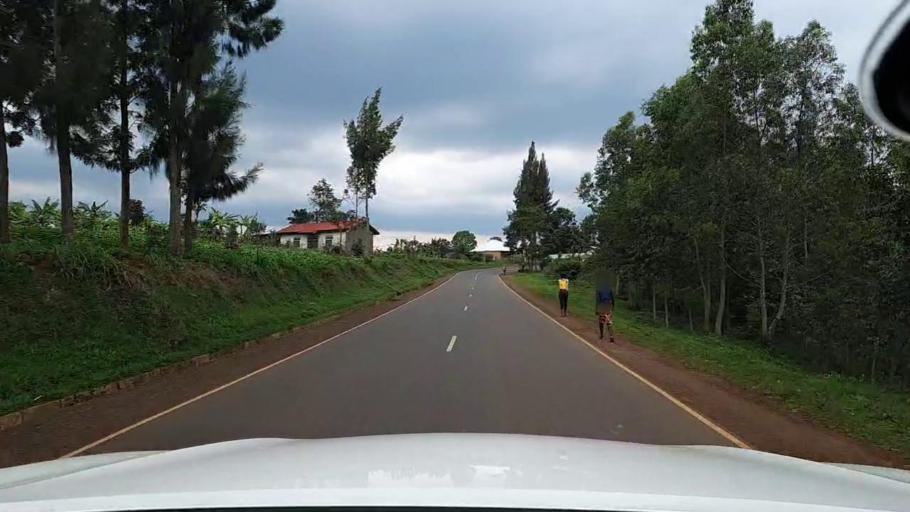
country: RW
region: Western Province
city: Cyangugu
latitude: -2.5938
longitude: 28.9287
